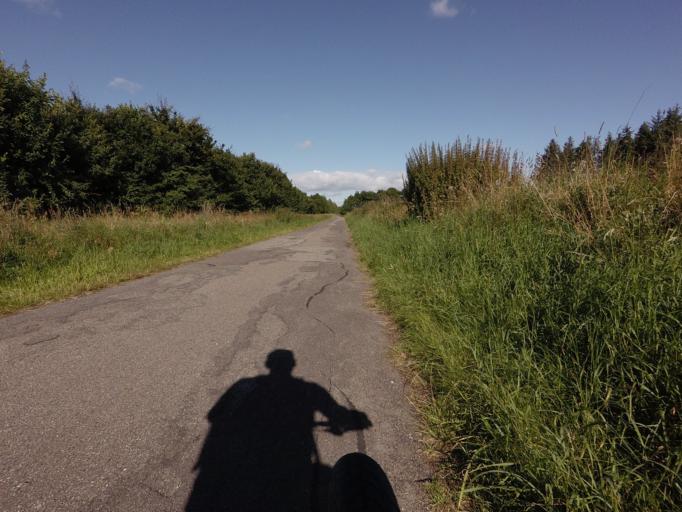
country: DK
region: Central Jutland
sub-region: Skanderborg Kommune
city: Ry
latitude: 55.9606
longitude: 9.7662
